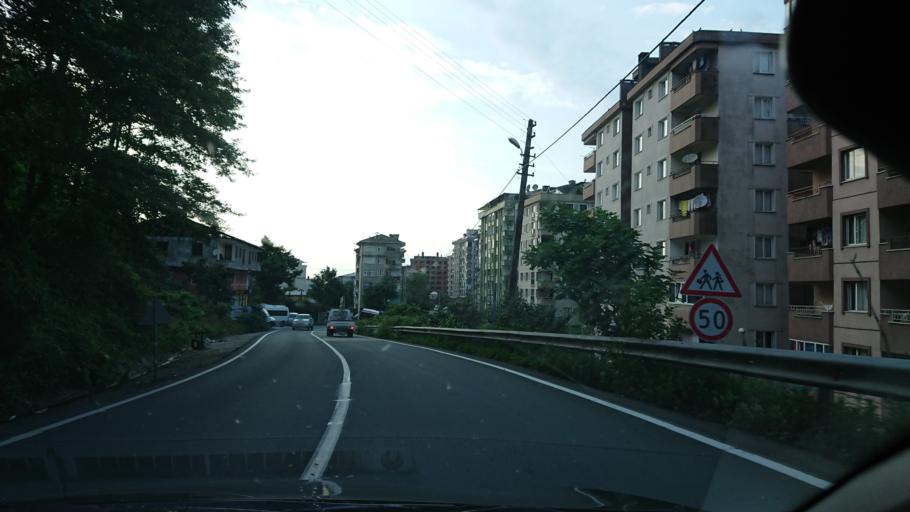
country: TR
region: Rize
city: Cayeli
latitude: 41.0795
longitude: 40.7132
